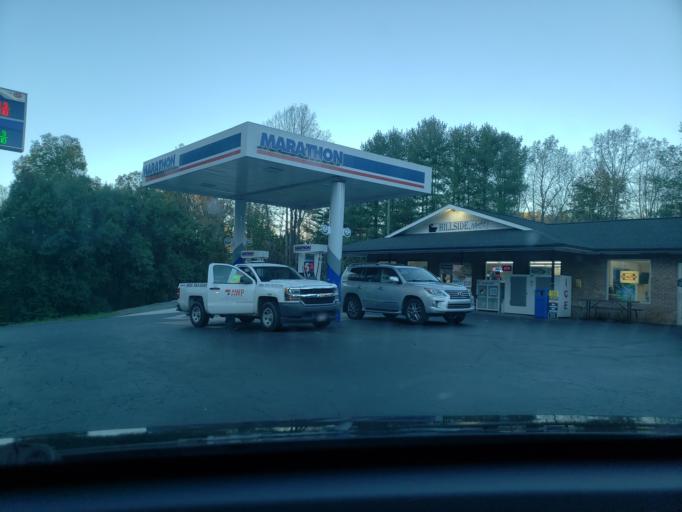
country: US
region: North Carolina
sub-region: Stokes County
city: Danbury
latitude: 36.4005
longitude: -80.2022
